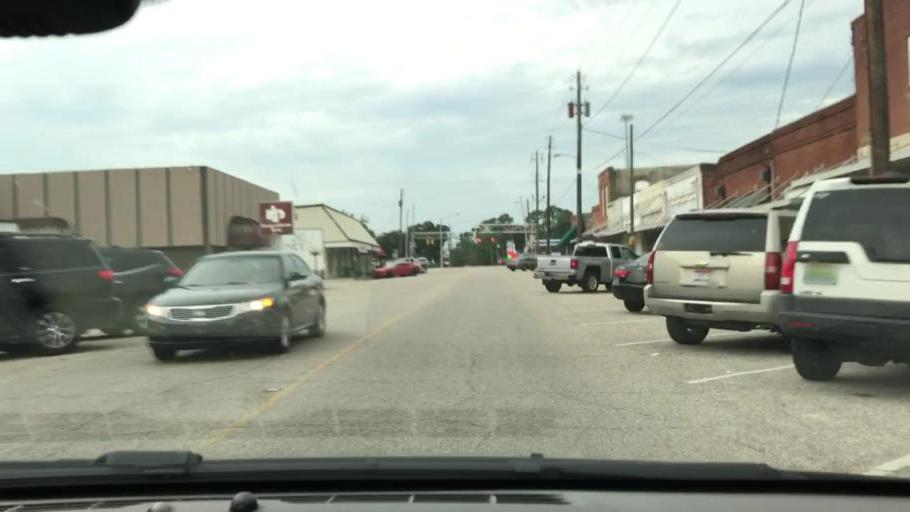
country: US
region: Alabama
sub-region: Houston County
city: Ashford
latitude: 31.1841
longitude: -85.2360
